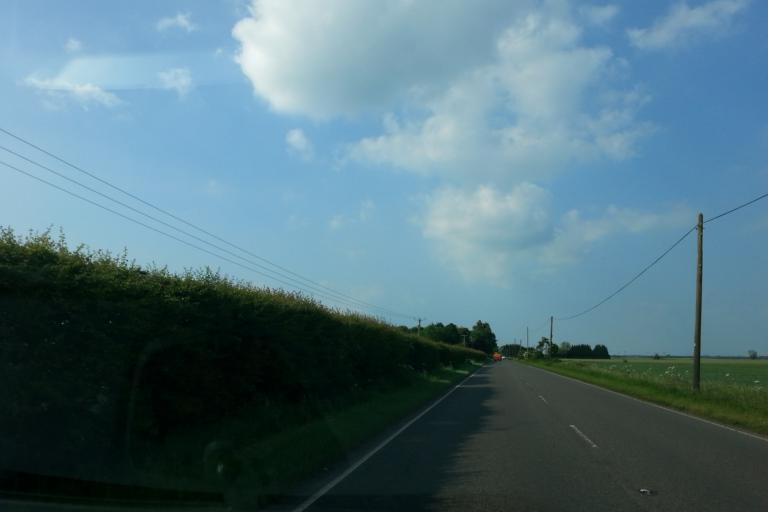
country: GB
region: England
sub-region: Cambridgeshire
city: Earith
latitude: 52.3253
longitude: 0.0623
